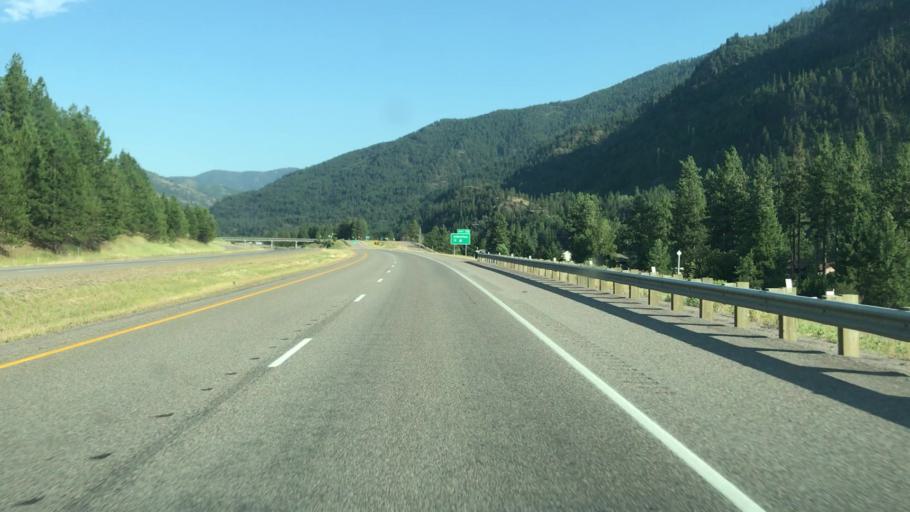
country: US
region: Montana
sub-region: Missoula County
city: Frenchtown
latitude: 47.0098
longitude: -114.5000
